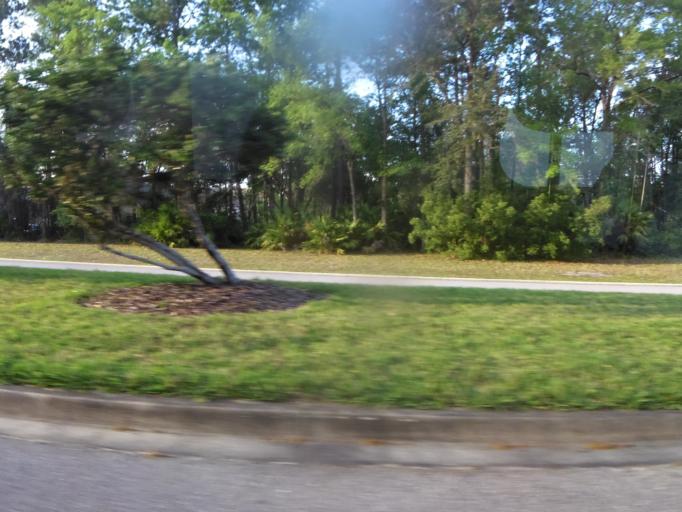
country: US
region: Florida
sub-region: Saint Johns County
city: Fruit Cove
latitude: 30.1172
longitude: -81.5751
